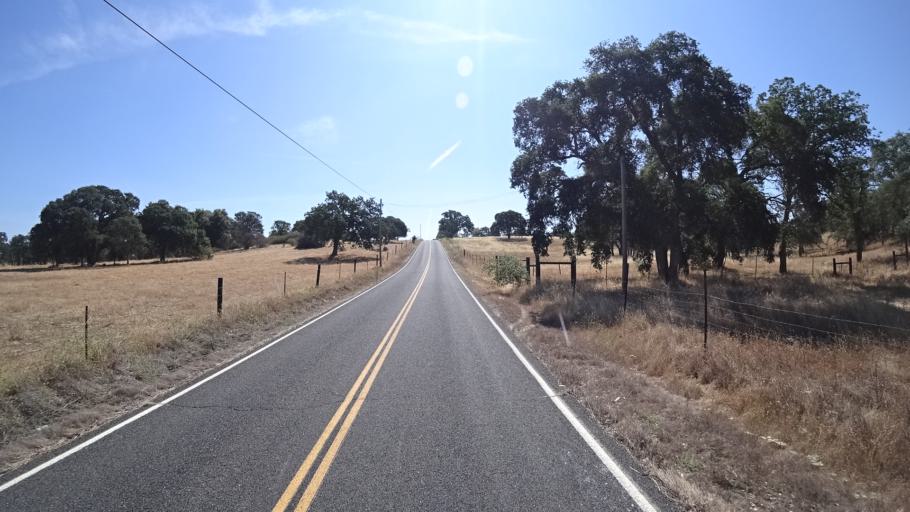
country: US
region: California
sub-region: Calaveras County
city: Rancho Calaveras
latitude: 38.1340
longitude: -120.9077
